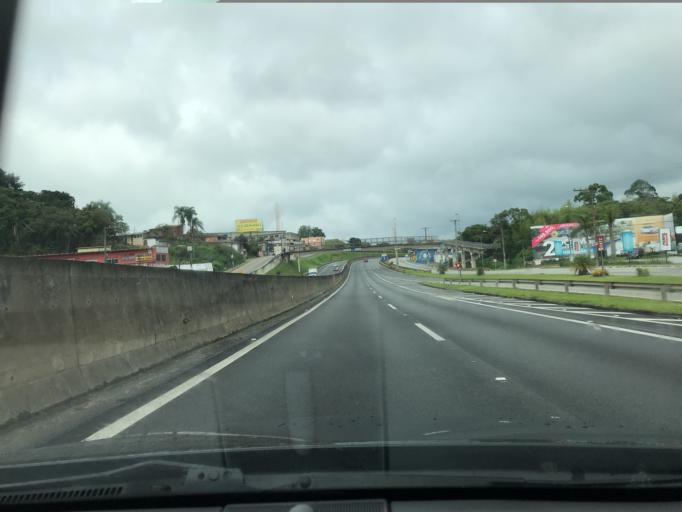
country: BR
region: Sao Paulo
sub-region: Vargem Grande Paulista
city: Vargem Grande Paulista
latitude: -23.6125
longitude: -47.0031
